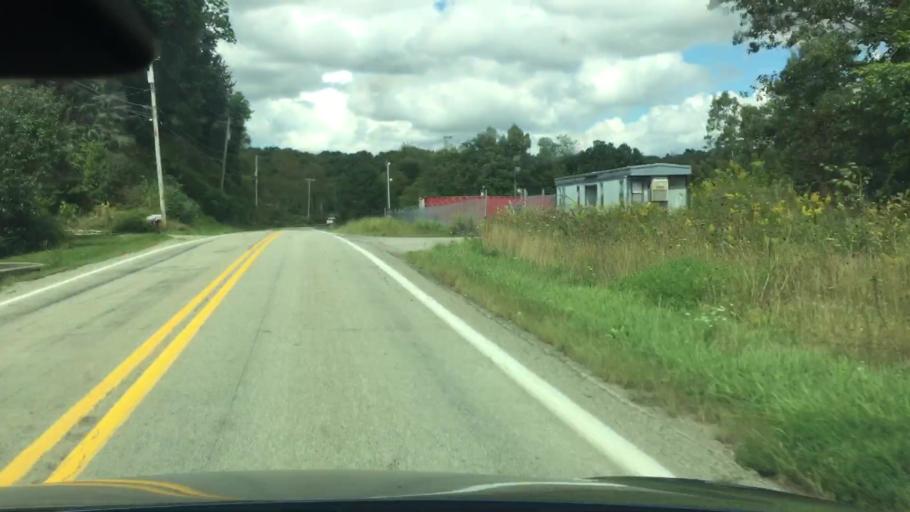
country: US
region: Pennsylvania
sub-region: Allegheny County
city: Curtisville
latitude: 40.6619
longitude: -79.8355
